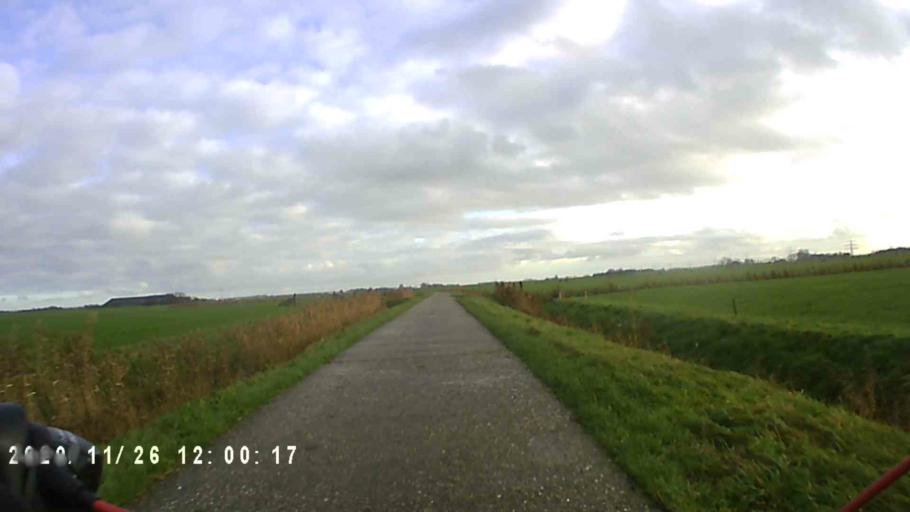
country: NL
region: Groningen
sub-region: Gemeente Bedum
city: Bedum
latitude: 53.3182
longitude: 6.6069
